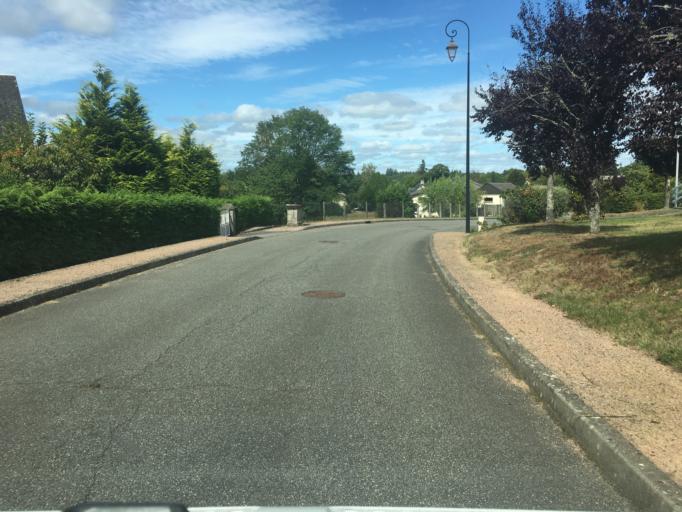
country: FR
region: Auvergne
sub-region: Departement du Cantal
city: Champagnac
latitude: 45.4203
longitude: 2.3840
